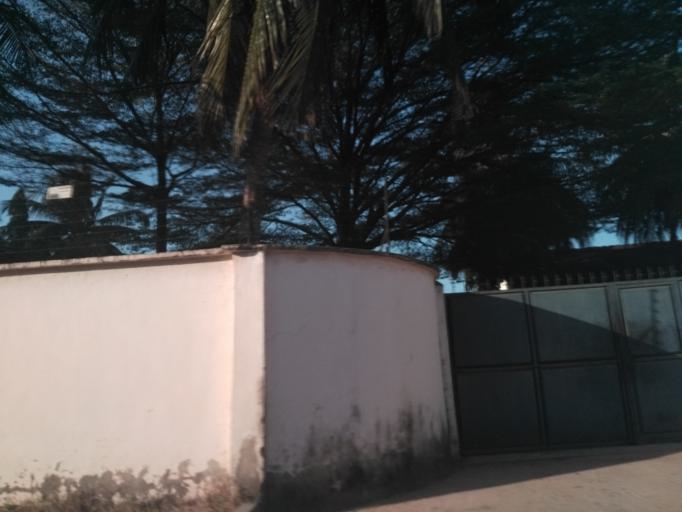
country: TZ
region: Dar es Salaam
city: Magomeni
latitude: -6.7608
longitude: 39.2562
